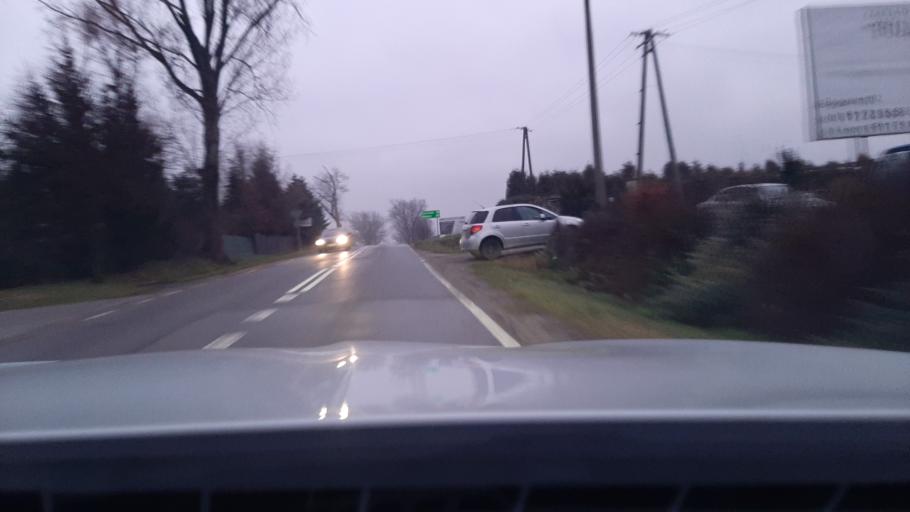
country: PL
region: Lublin Voivodeship
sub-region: Powiat lubelski
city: Garbow
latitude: 51.3448
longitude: 22.3638
